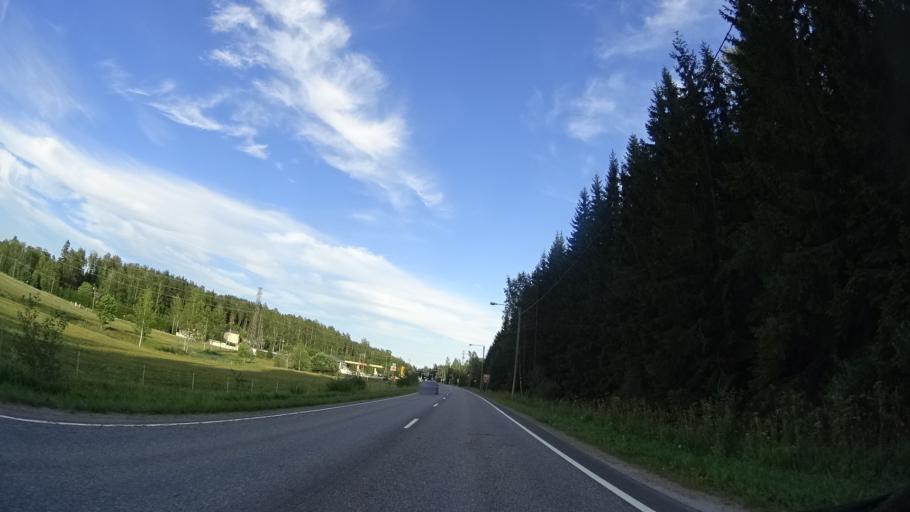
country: FI
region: Uusimaa
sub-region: Helsinki
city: Espoo
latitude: 60.1928
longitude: 24.5665
